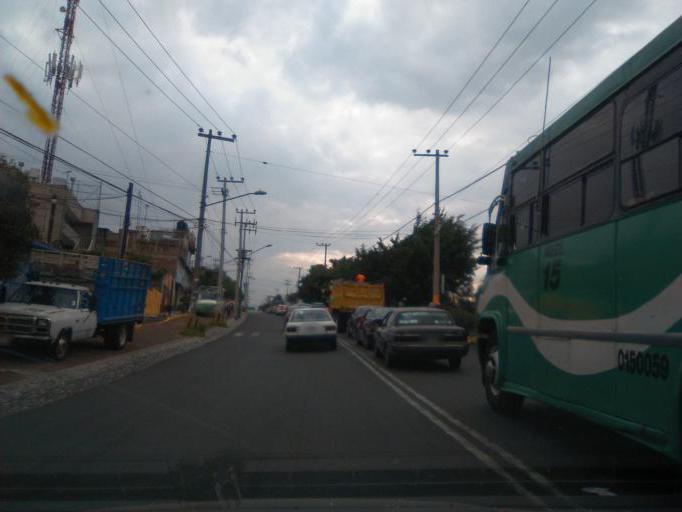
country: MX
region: Mexico City
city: Col. Bosques de las Lomas
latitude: 19.3658
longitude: -99.2430
